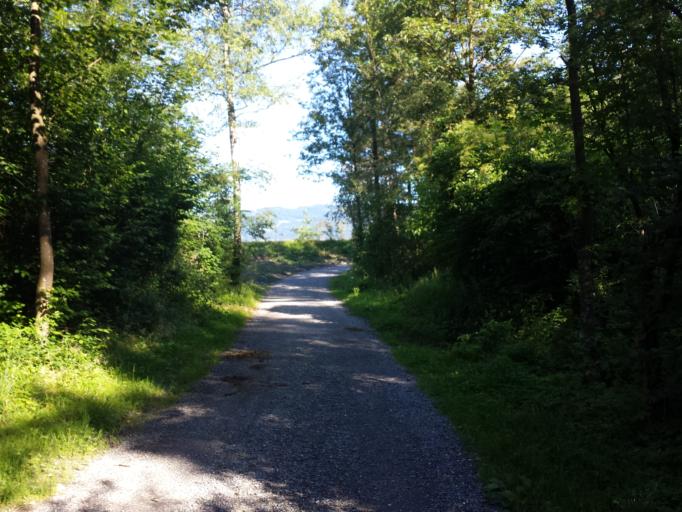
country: CH
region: Saint Gallen
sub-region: Wahlkreis Rheintal
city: Diepoldsau
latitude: 47.4036
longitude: 9.6537
